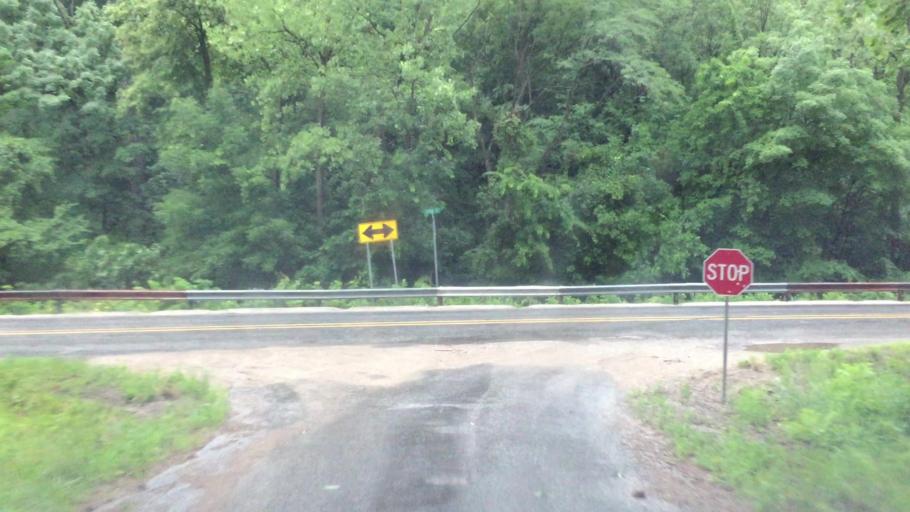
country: US
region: Iowa
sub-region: Lee County
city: Fort Madison
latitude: 40.6064
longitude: -91.2778
